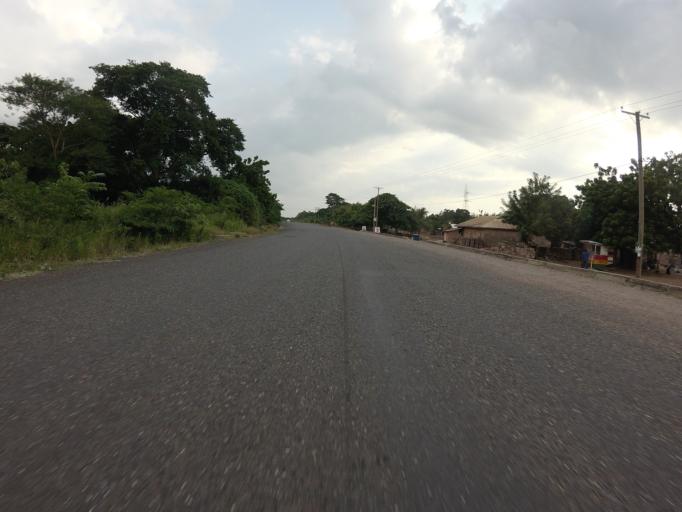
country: GH
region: Volta
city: Ho
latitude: 6.5050
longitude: 0.4895
